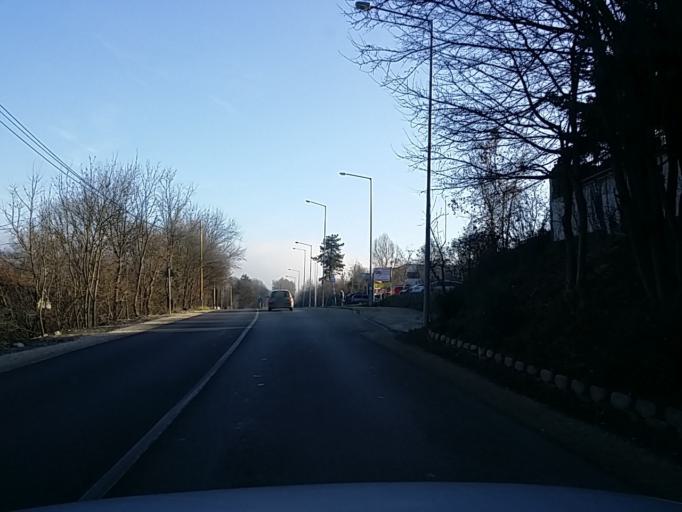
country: HU
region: Pest
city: Solymar
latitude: 47.5594
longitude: 18.9199
